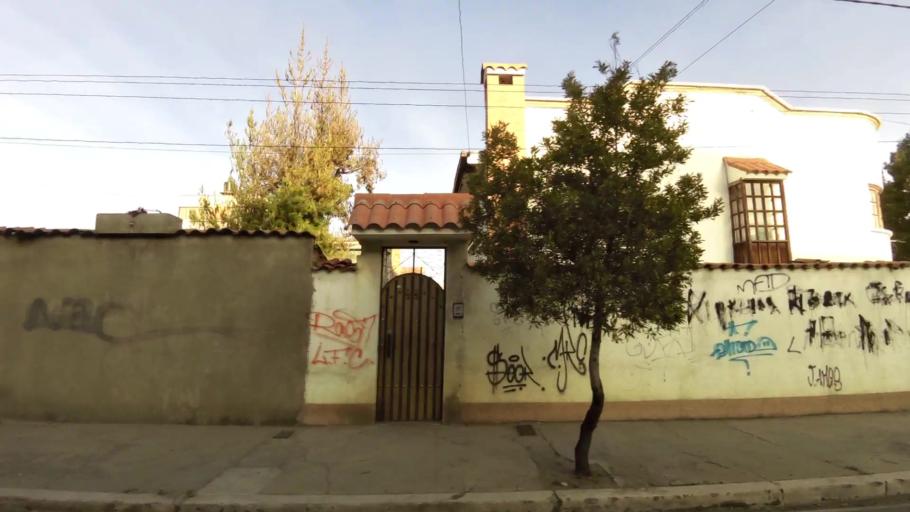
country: BO
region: La Paz
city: La Paz
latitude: -16.5208
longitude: -68.1116
